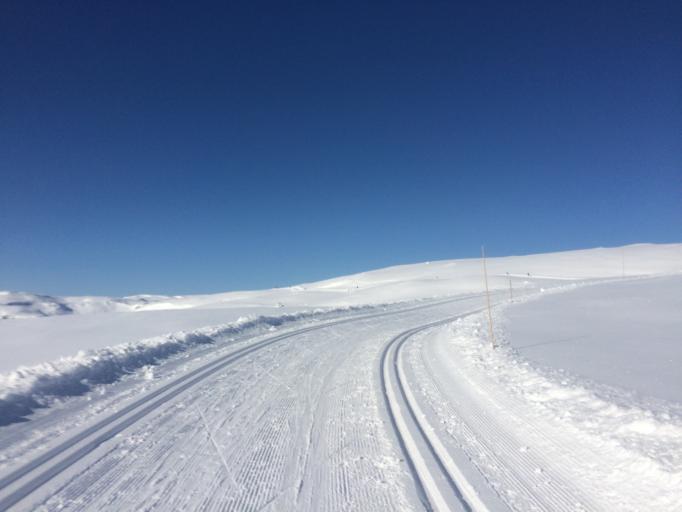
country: NO
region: Oppland
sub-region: Ringebu
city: Ringebu
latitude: 61.3683
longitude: 10.0743
